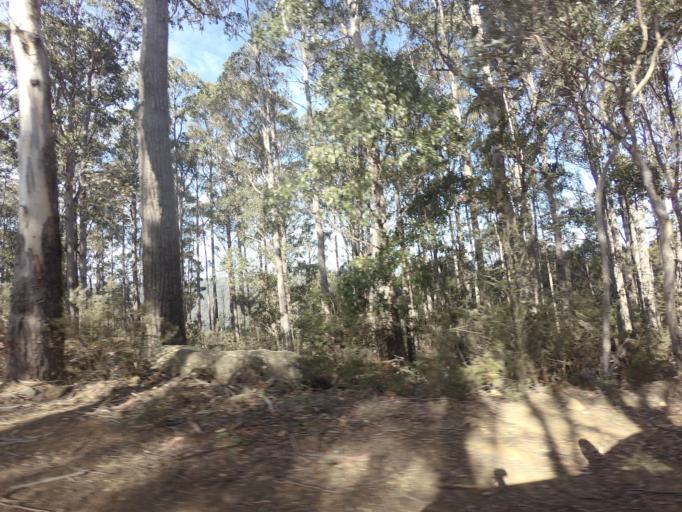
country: AU
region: Tasmania
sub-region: Sorell
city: Sorell
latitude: -42.4981
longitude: 147.4800
